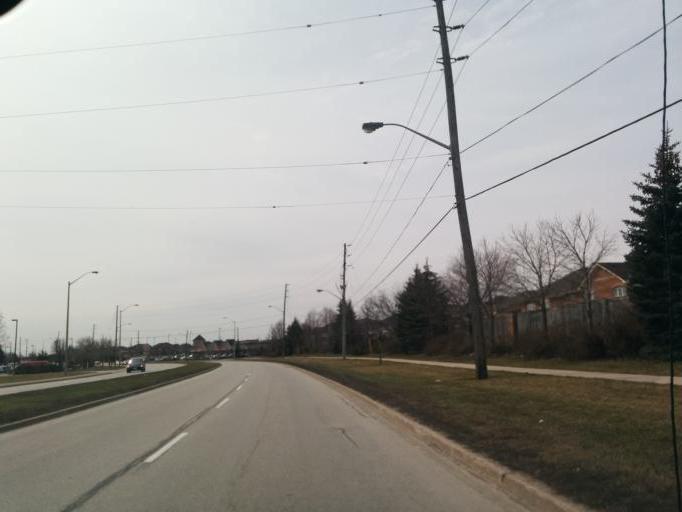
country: CA
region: Ontario
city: Brampton
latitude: 43.7123
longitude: -79.8091
